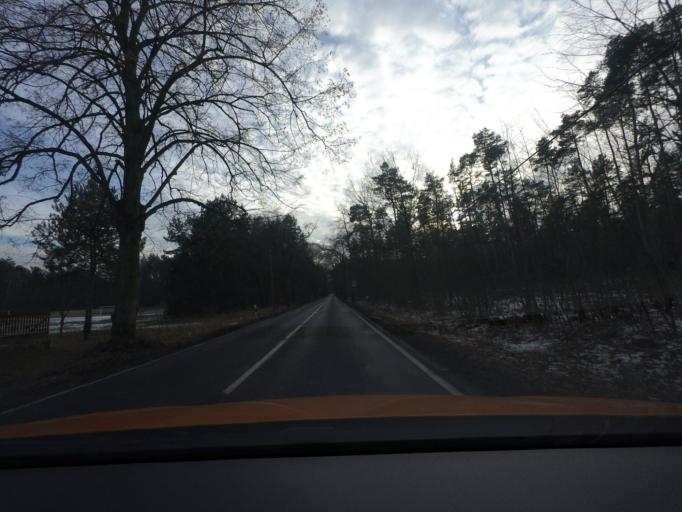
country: DE
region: Brandenburg
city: Wandlitz
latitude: 52.7481
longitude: 13.3738
